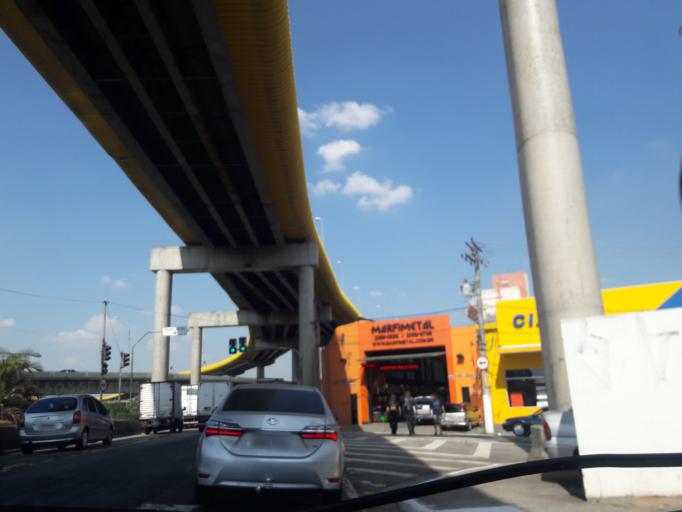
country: BR
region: Sao Paulo
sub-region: Sao Paulo
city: Sao Paulo
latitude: -23.5860
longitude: -46.5989
